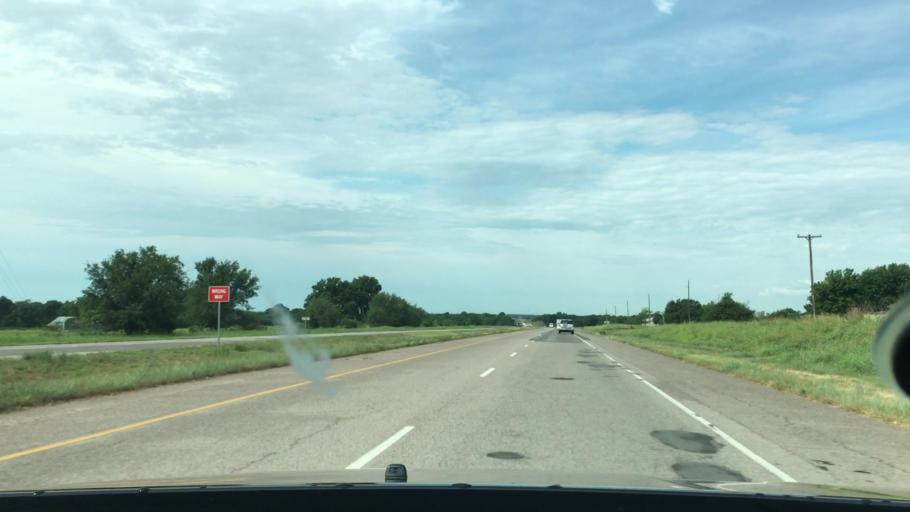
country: US
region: Oklahoma
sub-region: Pontotoc County
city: Ada
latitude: 34.6753
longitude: -96.7753
